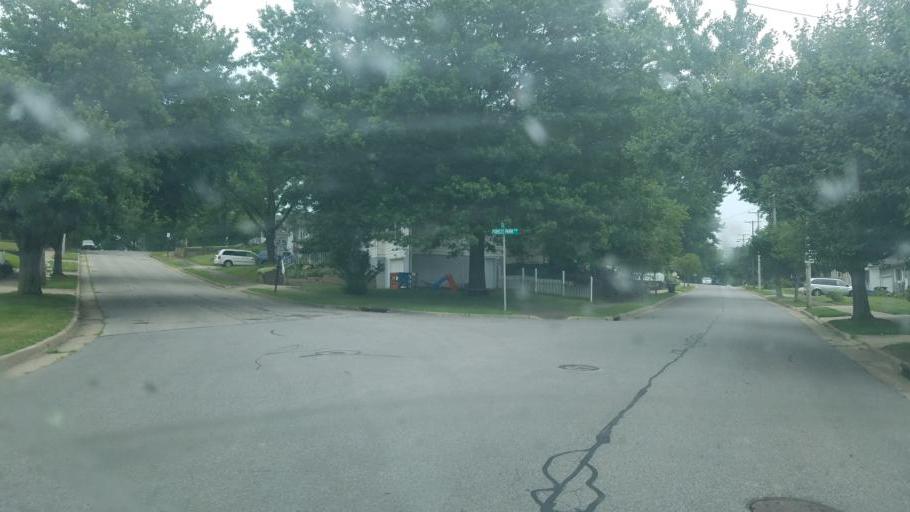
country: US
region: Ohio
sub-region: Summit County
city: Sawyerwood
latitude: 41.0549
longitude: -81.4249
